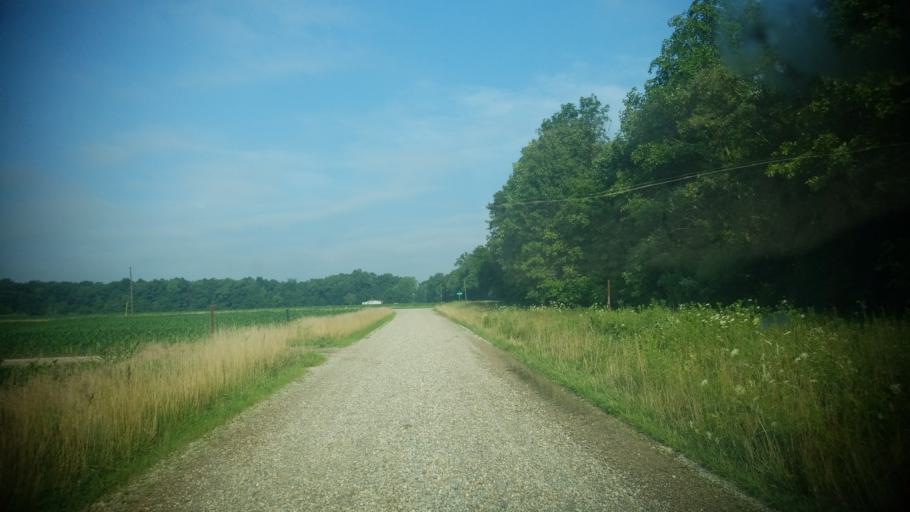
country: US
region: Illinois
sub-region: Clay County
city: Flora
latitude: 38.6022
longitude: -88.3627
